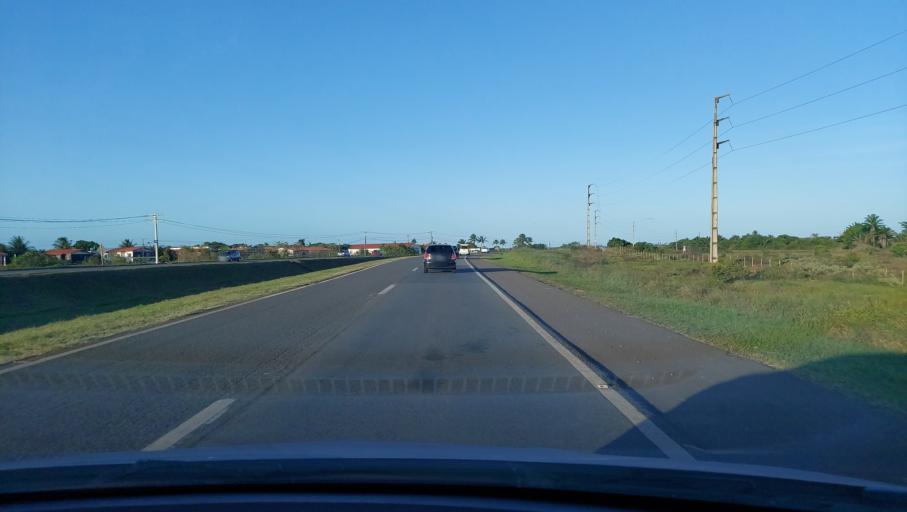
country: BR
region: Bahia
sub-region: Camacari
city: Camacari
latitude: -12.7557
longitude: -38.1768
